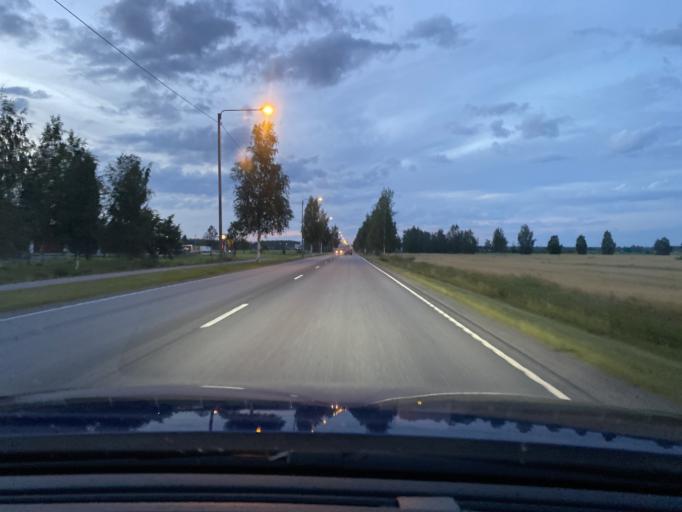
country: FI
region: Southern Ostrobothnia
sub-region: Suupohja
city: Kauhajoki
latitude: 62.4360
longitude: 22.2069
